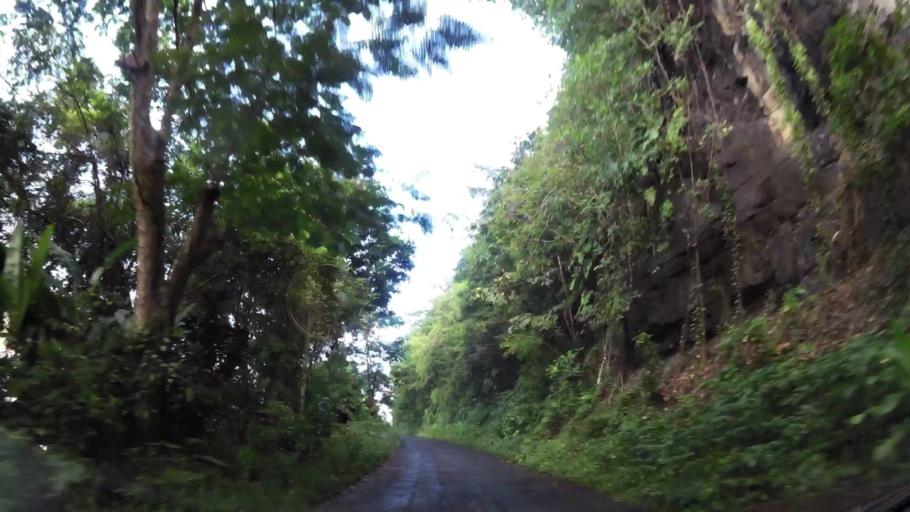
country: DM
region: Saint Andrew
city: Marigot
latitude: 15.5165
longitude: -61.2724
